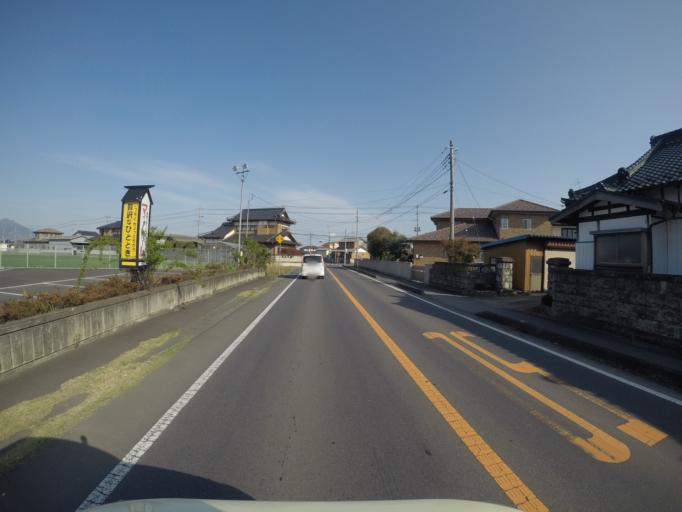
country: JP
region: Ibaraki
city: Ishige
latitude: 36.1950
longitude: 139.9767
